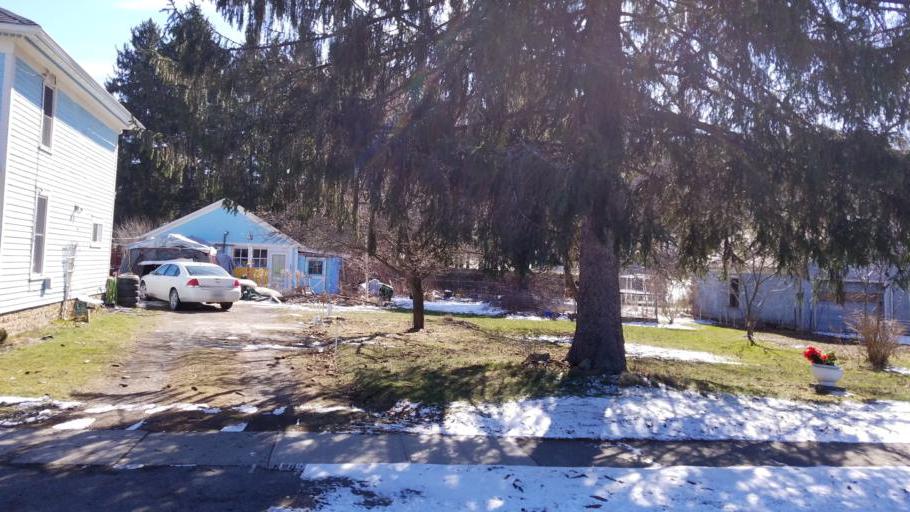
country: US
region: New York
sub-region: Allegany County
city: Wellsville
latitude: 42.1231
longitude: -77.9600
